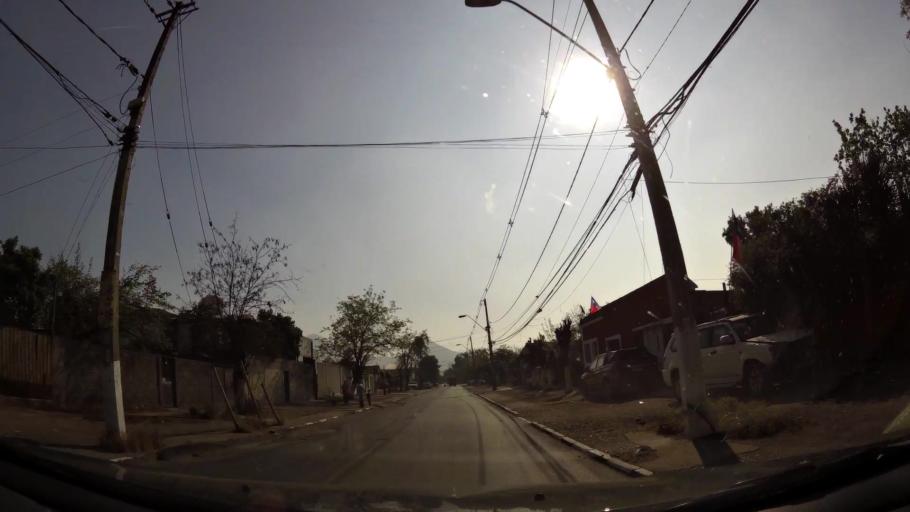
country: CL
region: Santiago Metropolitan
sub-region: Provincia de Santiago
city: Santiago
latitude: -33.3845
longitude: -70.6749
